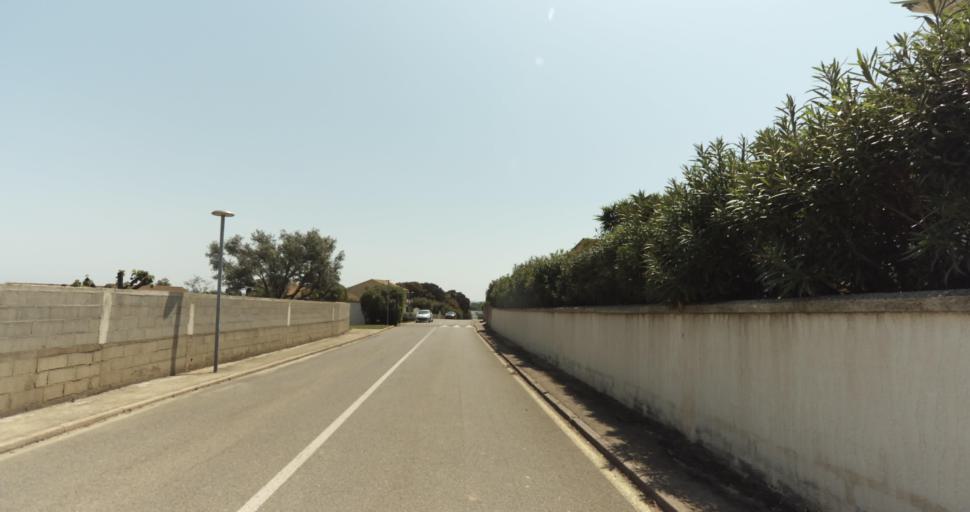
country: FR
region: Corsica
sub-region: Departement de la Haute-Corse
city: Biguglia
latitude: 42.6063
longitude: 9.4316
